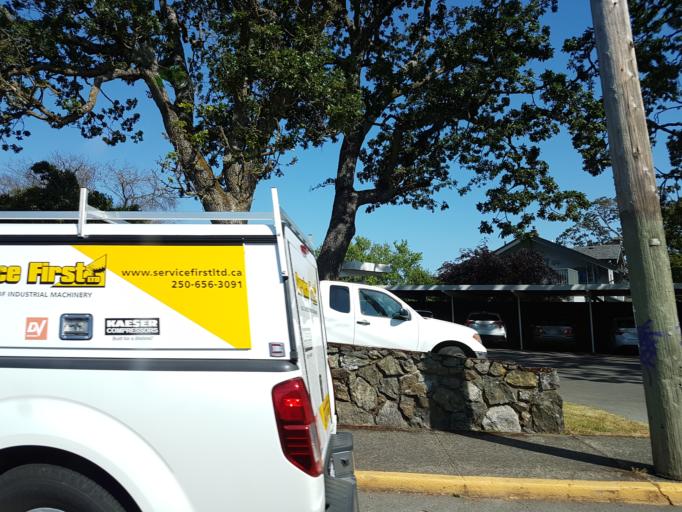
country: CA
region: British Columbia
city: Victoria
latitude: 48.4289
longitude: -123.3369
